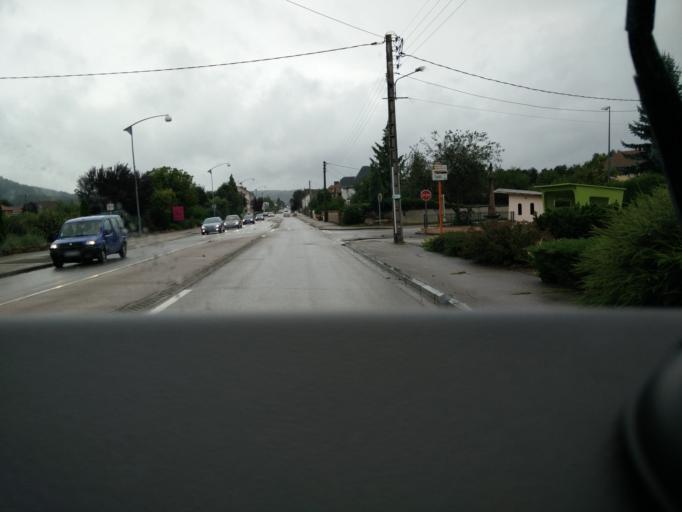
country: FR
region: Lorraine
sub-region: Departement des Vosges
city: Anould
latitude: 48.1896
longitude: 6.9525
